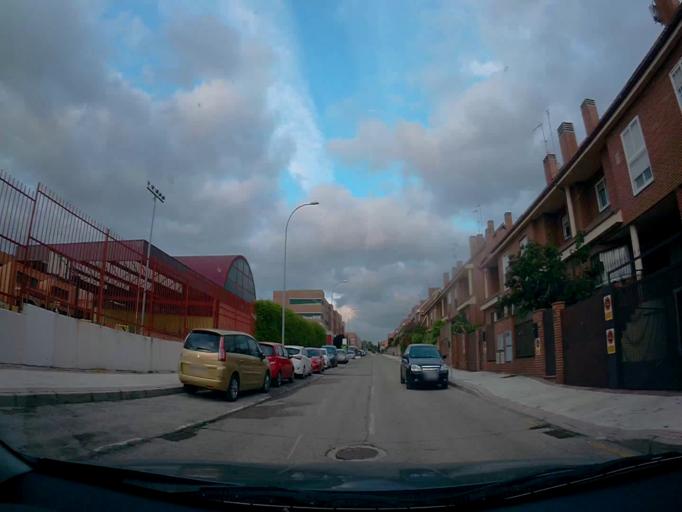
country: ES
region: Madrid
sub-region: Provincia de Madrid
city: Alcorcon
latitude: 40.3345
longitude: -3.8302
